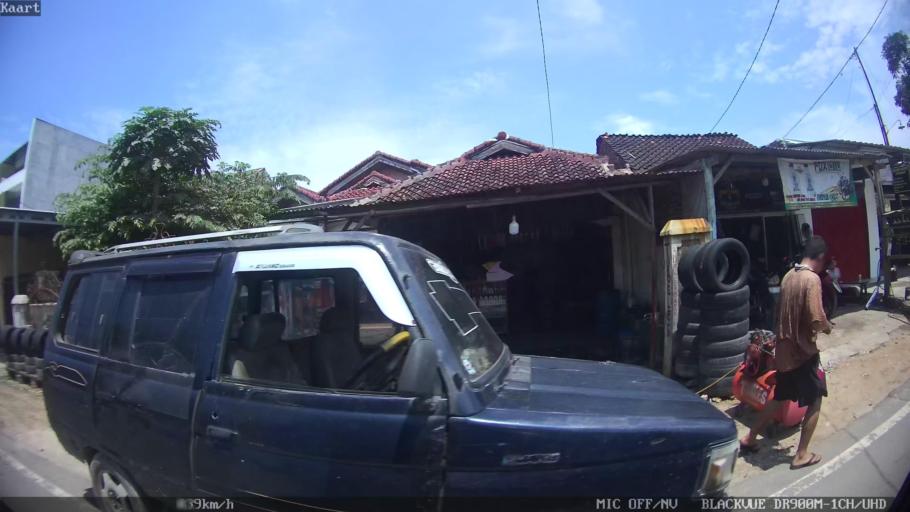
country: ID
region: Lampung
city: Kedaton
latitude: -5.3661
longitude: 105.2895
